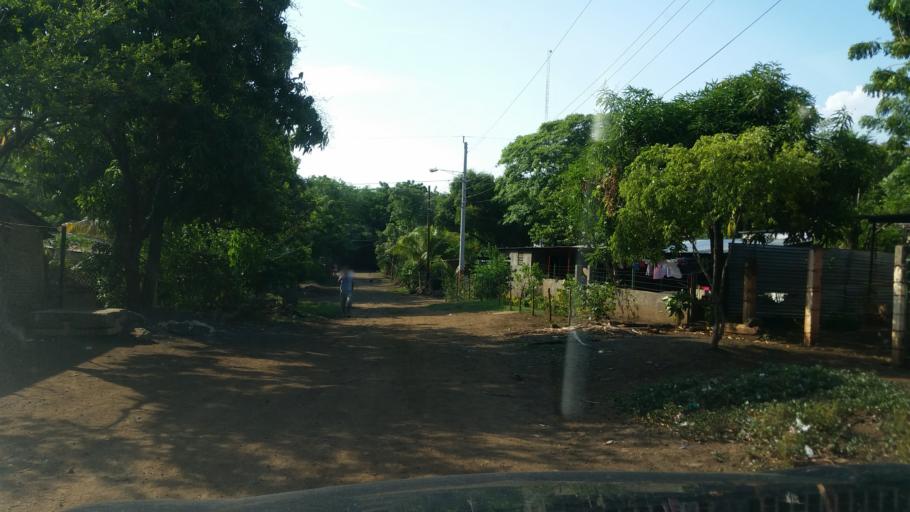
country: NI
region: Managua
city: Masachapa
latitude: 11.7894
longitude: -86.5147
